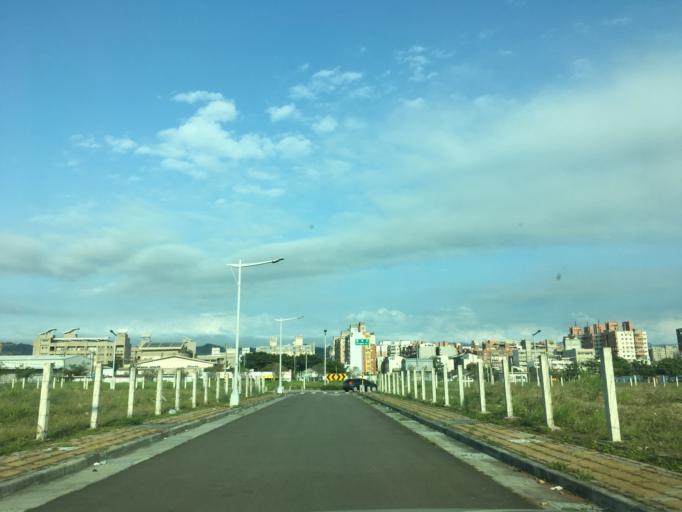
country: TW
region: Taiwan
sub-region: Taichung City
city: Taichung
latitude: 24.1960
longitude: 120.6916
